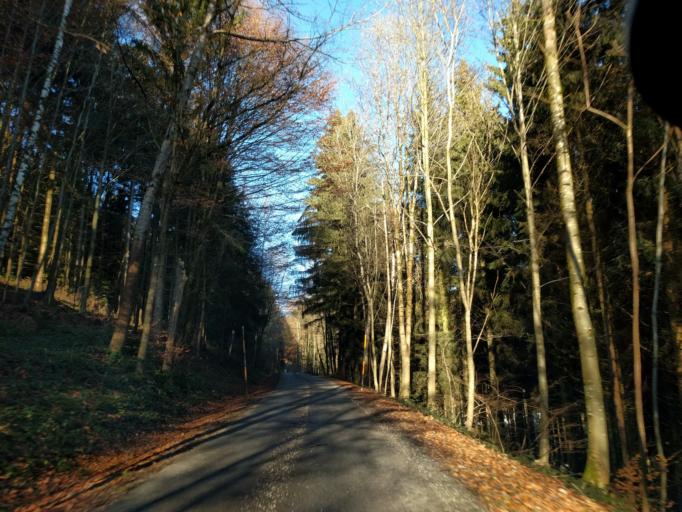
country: AT
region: Upper Austria
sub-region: Politischer Bezirk Urfahr-Umgebung
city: Kirchschlag bei Linz
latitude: 48.4121
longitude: 14.2894
